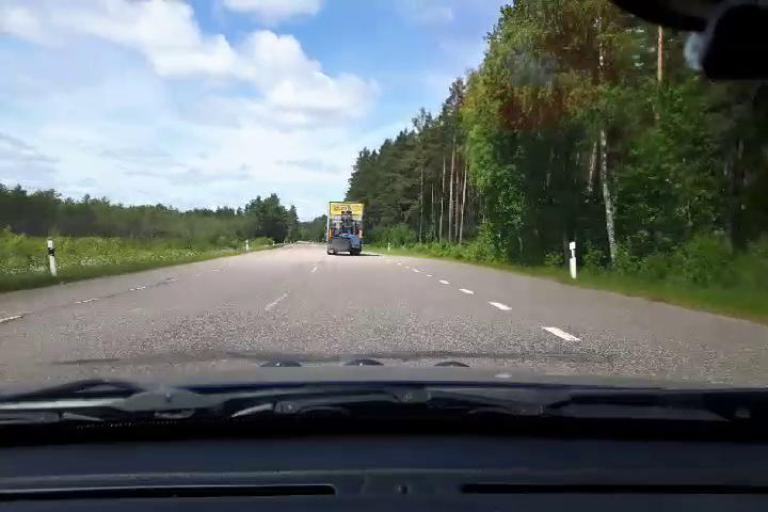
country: SE
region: Uppsala
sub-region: Osthammars Kommun
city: Bjorklinge
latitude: 60.1009
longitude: 17.5525
